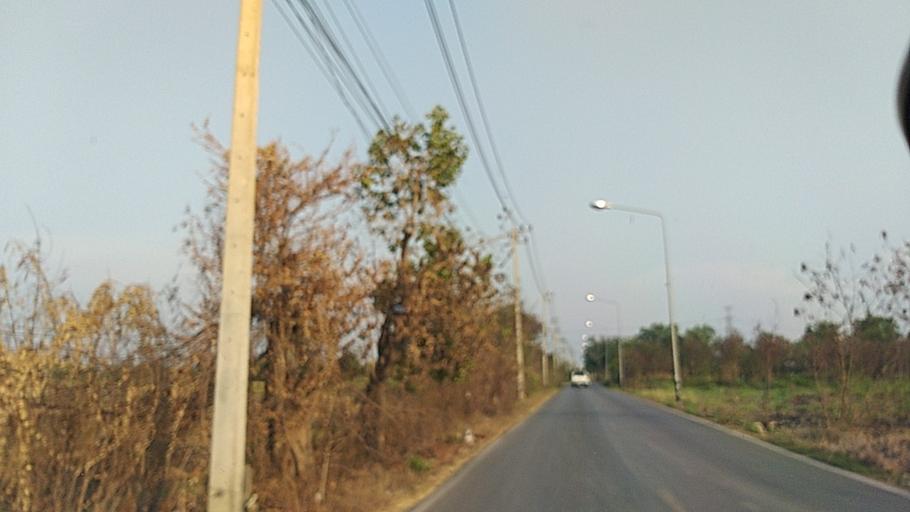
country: TH
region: Sara Buri
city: Nong Khae
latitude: 14.2832
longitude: 100.8154
